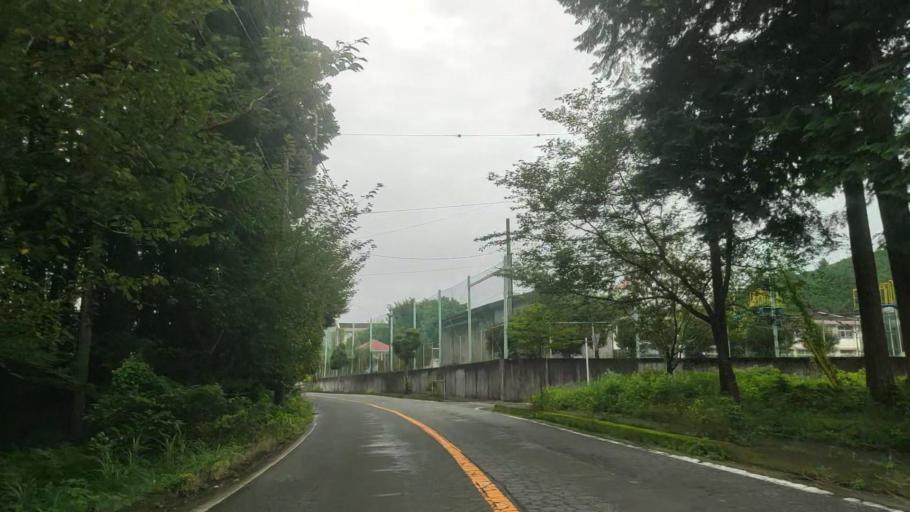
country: JP
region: Shizuoka
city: Fujinomiya
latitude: 35.2080
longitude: 138.5909
